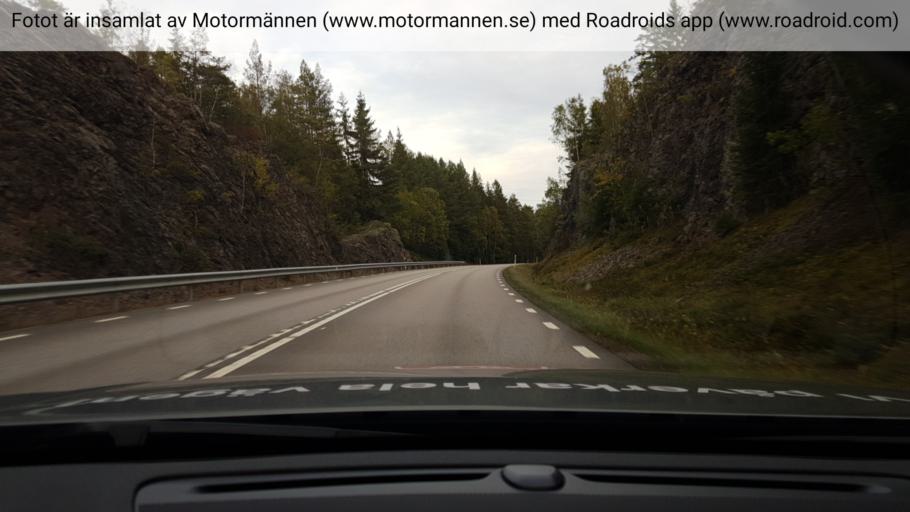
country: SE
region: Vaestra Goetaland
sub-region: Bengtsfors Kommun
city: Dals Langed
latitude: 59.0279
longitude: 12.3930
